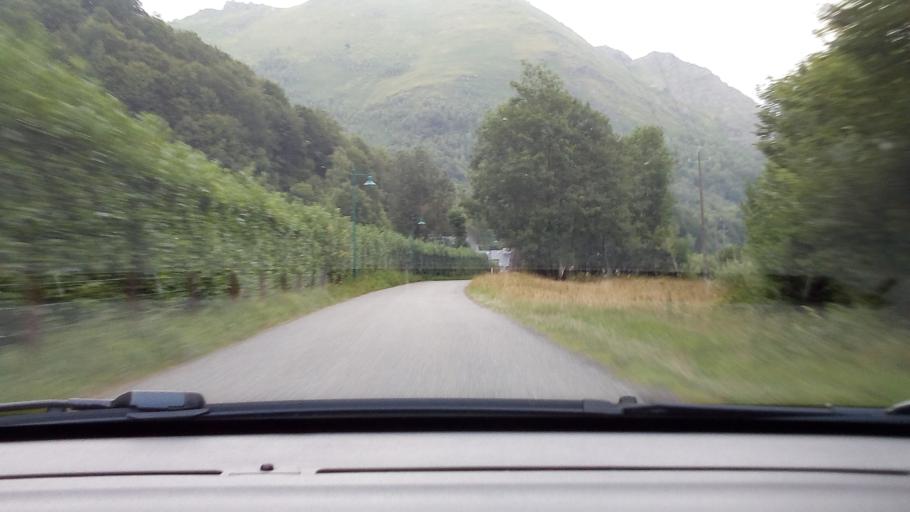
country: FR
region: Midi-Pyrenees
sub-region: Departement des Hautes-Pyrenees
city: Cauterets
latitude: 42.9376
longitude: -0.1783
